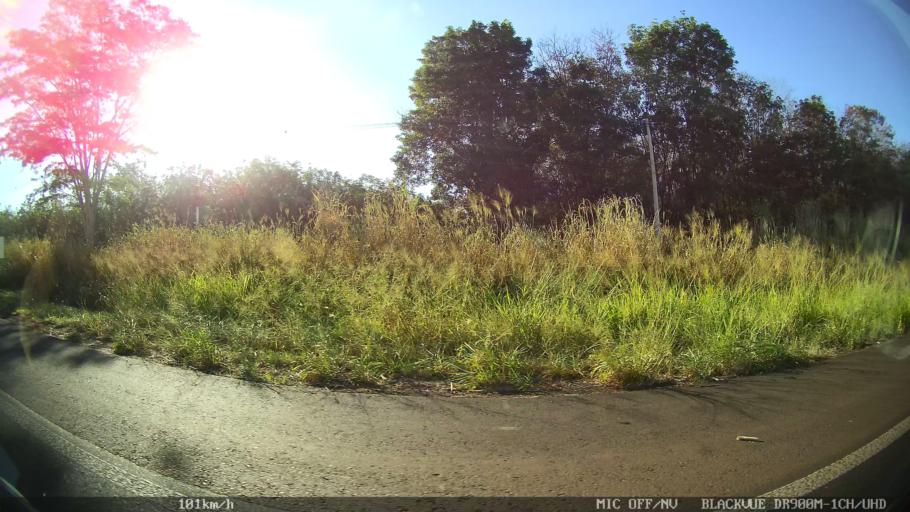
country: BR
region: Sao Paulo
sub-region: Olimpia
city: Olimpia
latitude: -20.7256
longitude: -49.0356
